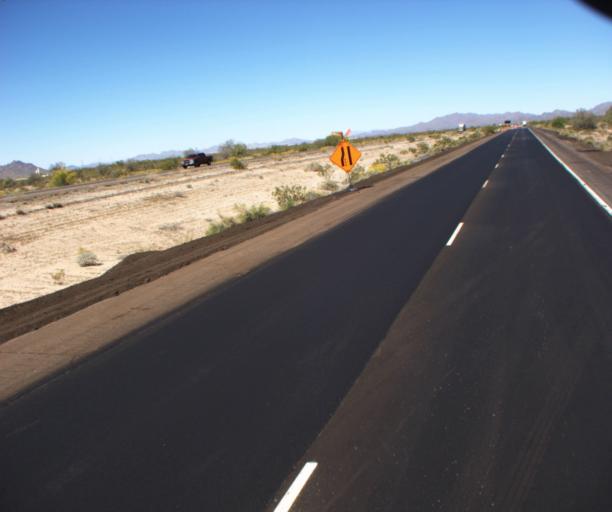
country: US
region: Arizona
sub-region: Maricopa County
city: Gila Bend
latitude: 32.9925
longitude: -112.6627
